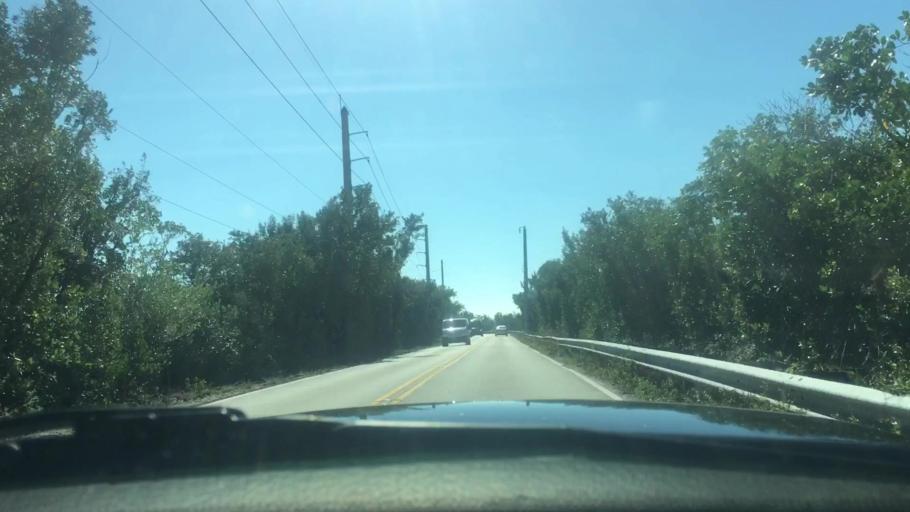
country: US
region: Florida
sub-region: Monroe County
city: North Key Largo
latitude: 25.2988
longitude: -80.3862
